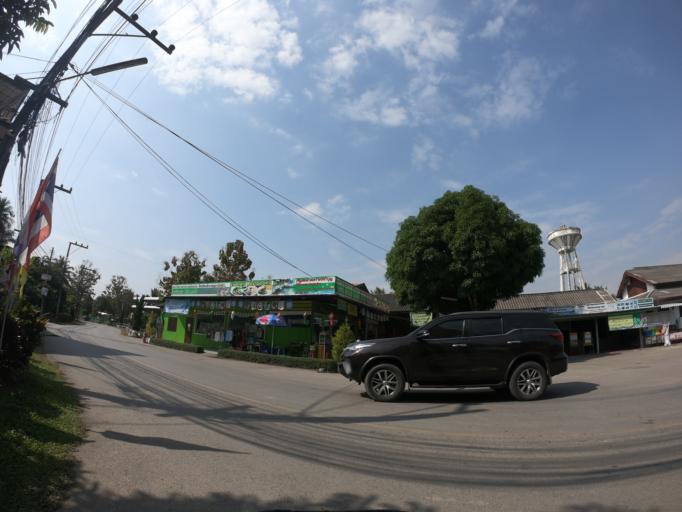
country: TH
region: Chiang Mai
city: Saraphi
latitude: 18.7035
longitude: 99.0602
